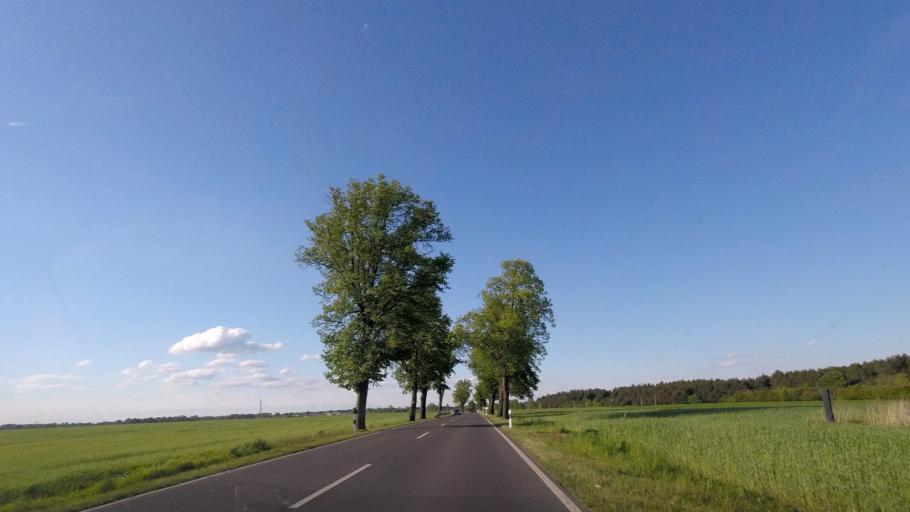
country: DE
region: Brandenburg
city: Luebben
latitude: 51.9142
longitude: 13.8949
